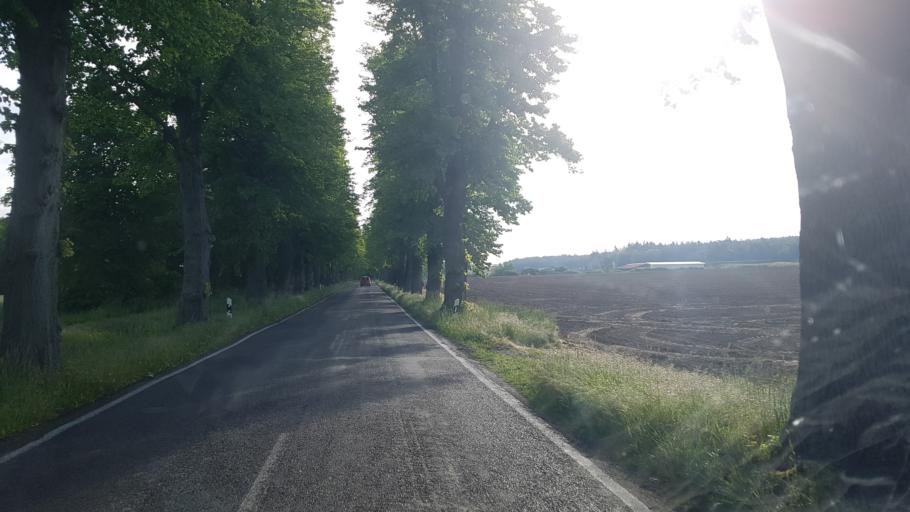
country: DE
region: Brandenburg
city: Dahme
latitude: 51.8961
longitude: 13.4798
